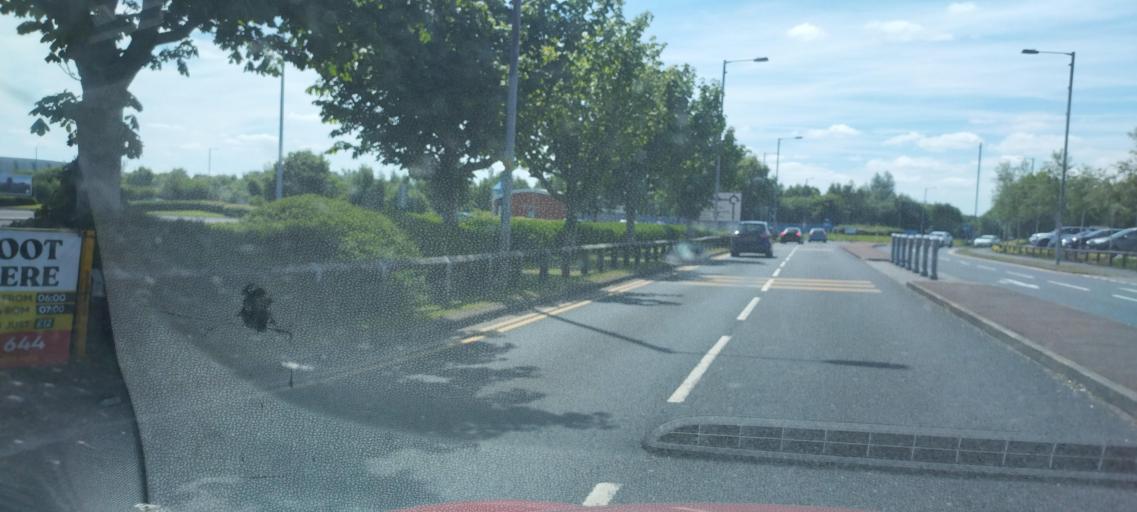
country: GB
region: England
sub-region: Borough of Bolton
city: Horwich
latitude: 53.5829
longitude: -2.5400
